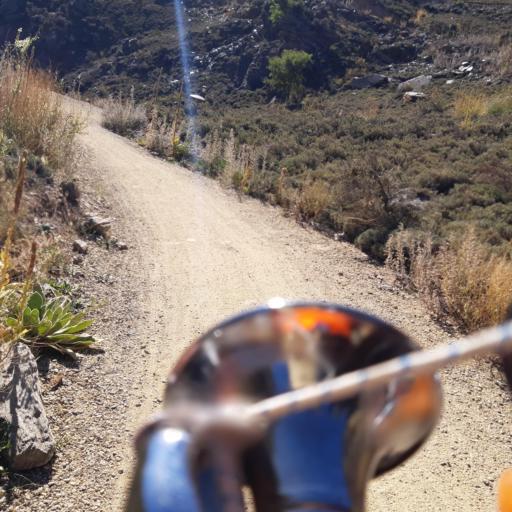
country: NZ
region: Otago
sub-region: Queenstown-Lakes District
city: Wanaka
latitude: -45.1077
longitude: 169.2919
